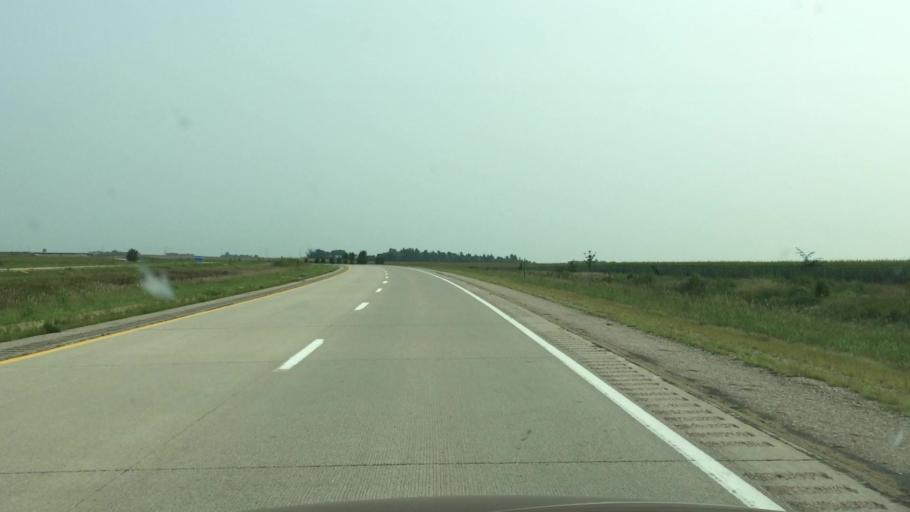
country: US
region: Iowa
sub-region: Osceola County
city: Sibley
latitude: 43.3909
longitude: -95.7188
